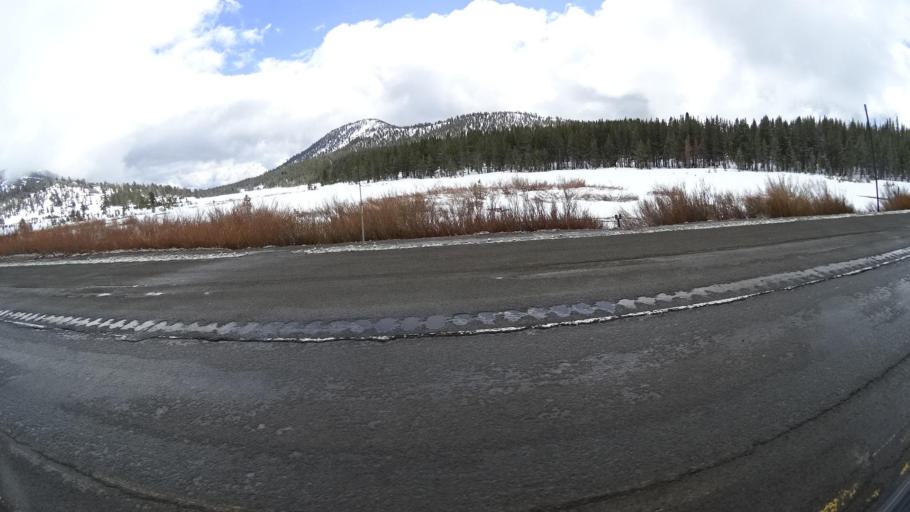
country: US
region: Nevada
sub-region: Washoe County
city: Incline Village
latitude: 39.3031
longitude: -119.9189
